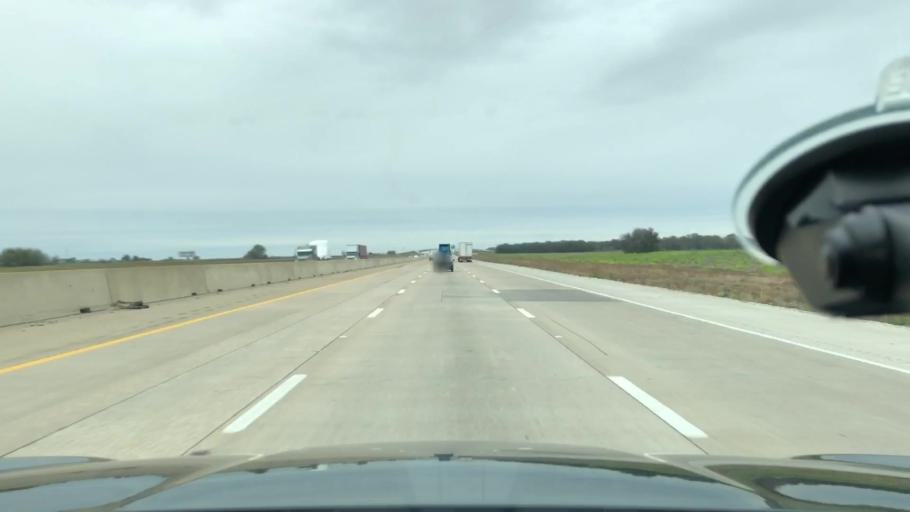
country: US
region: Texas
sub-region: Ellis County
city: Italy
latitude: 32.2472
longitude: -96.8754
